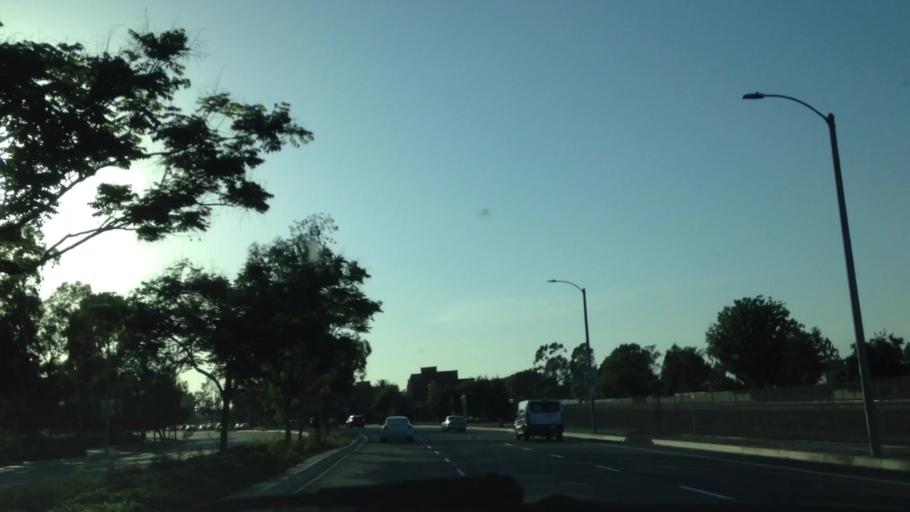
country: US
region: California
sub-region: Orange County
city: Tustin
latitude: 33.7196
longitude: -117.8231
